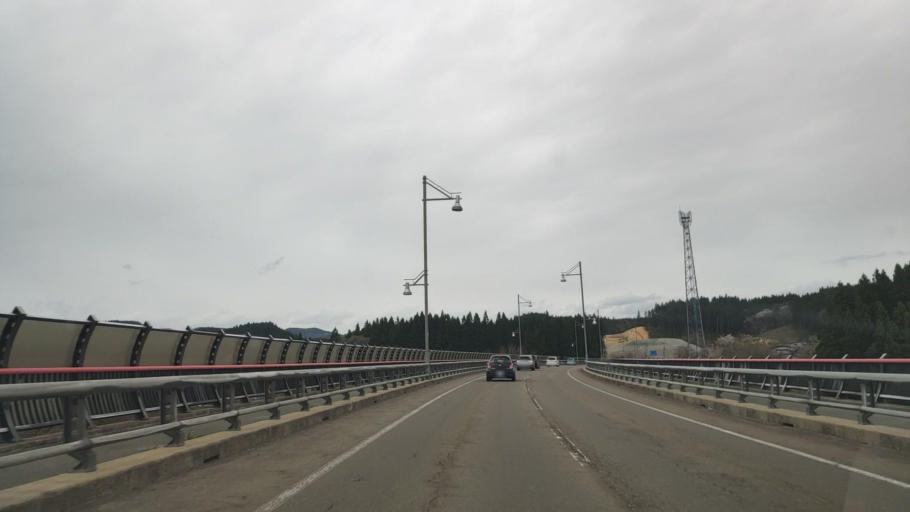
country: JP
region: Akita
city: Takanosu
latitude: 40.2097
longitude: 140.3021
